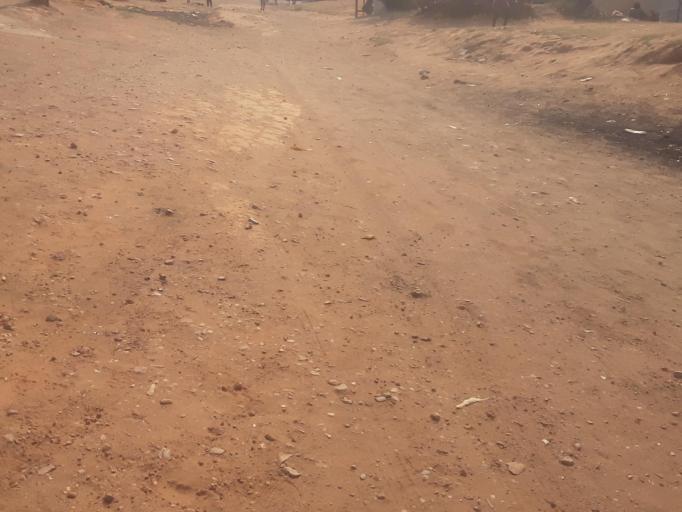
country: ZM
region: Lusaka
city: Lusaka
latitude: -15.3570
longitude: 28.2924
